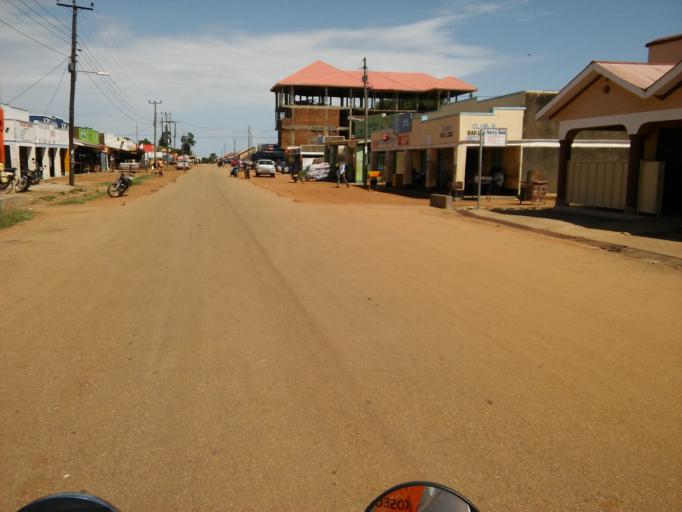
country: UG
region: Eastern Region
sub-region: Kumi District
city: Kumi
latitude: 1.4872
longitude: 33.9316
